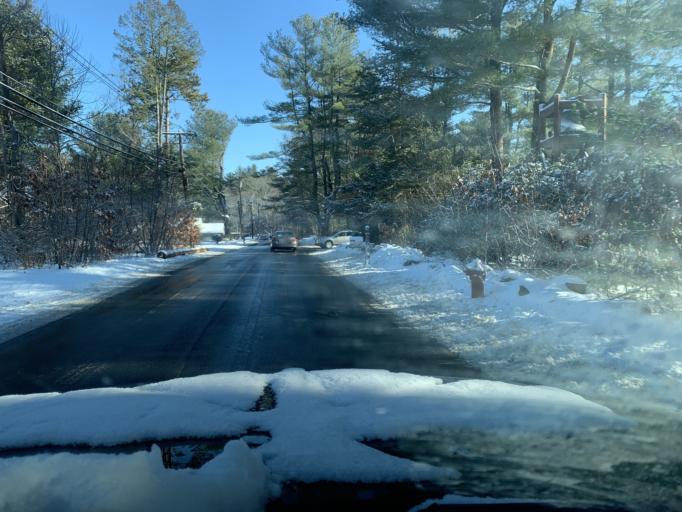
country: US
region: Massachusetts
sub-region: Essex County
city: Topsfield
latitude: 42.6339
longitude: -70.9678
